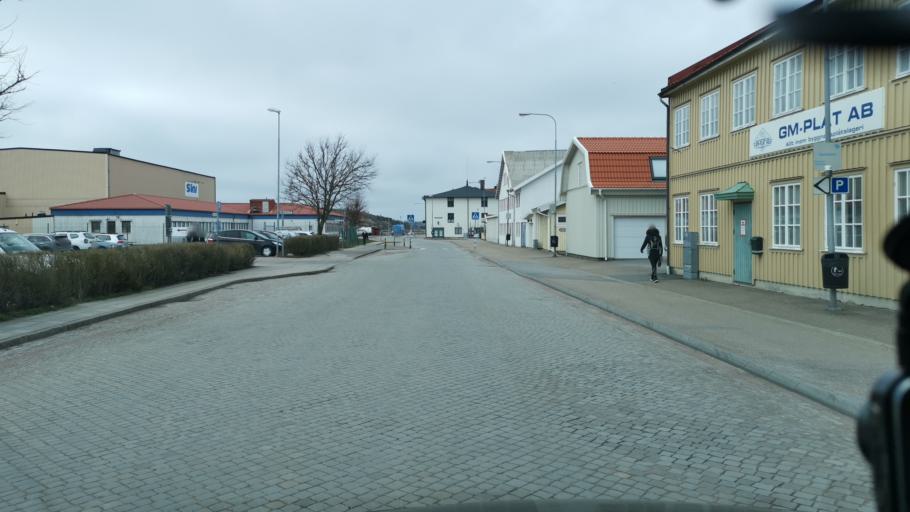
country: SE
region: Vaestra Goetaland
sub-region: Lysekils Kommun
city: Lysekil
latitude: 58.2747
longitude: 11.4279
